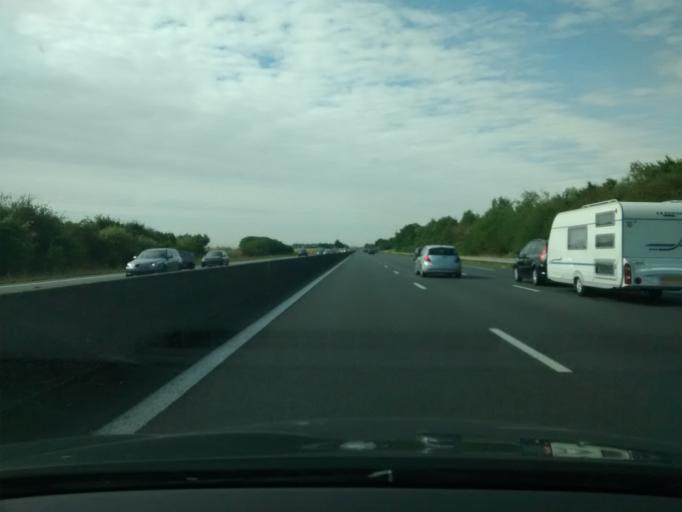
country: FR
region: Ile-de-France
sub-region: Departement de l'Essonne
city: Corbreuse
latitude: 48.4422
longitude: 1.9082
